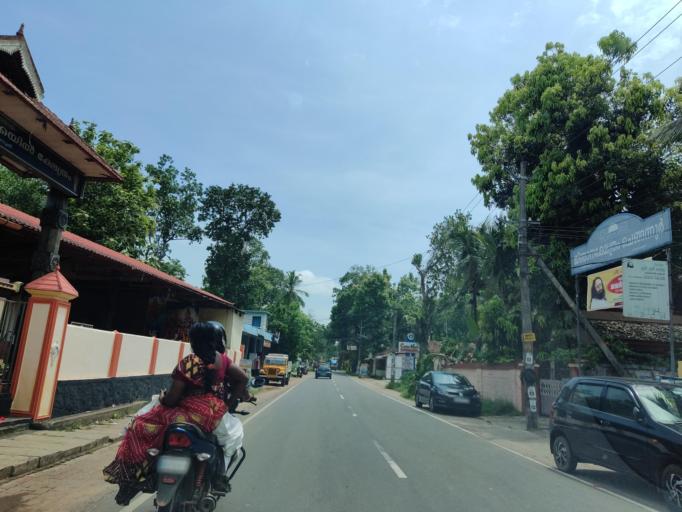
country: IN
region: Kerala
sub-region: Alappuzha
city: Chengannur
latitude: 9.3099
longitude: 76.5994
